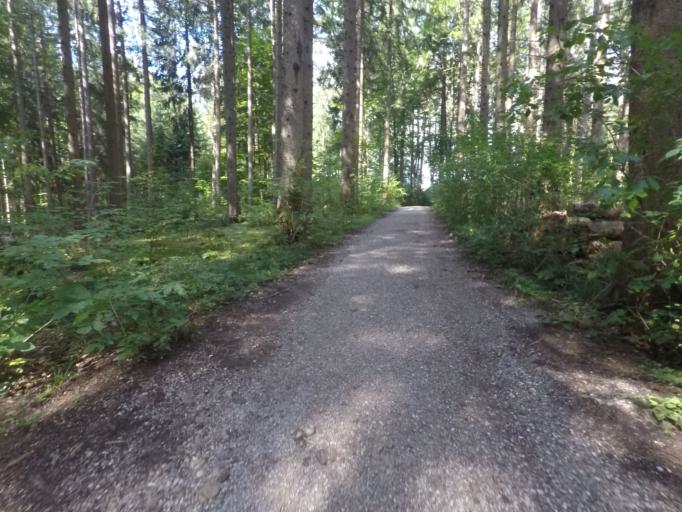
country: DE
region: Bavaria
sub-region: Upper Bavaria
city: Konigsdorf
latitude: 47.8293
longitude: 11.5092
